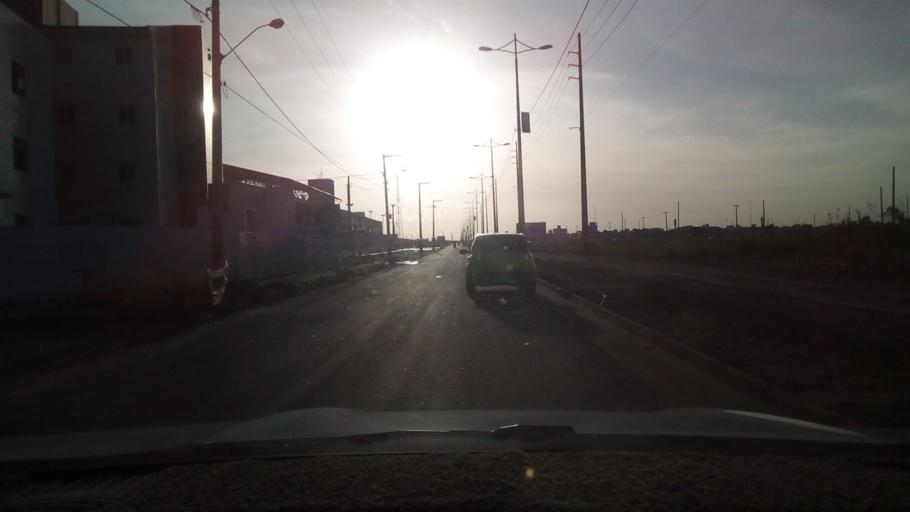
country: BR
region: Paraiba
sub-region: Conde
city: Conde
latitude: -7.1990
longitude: -34.8663
